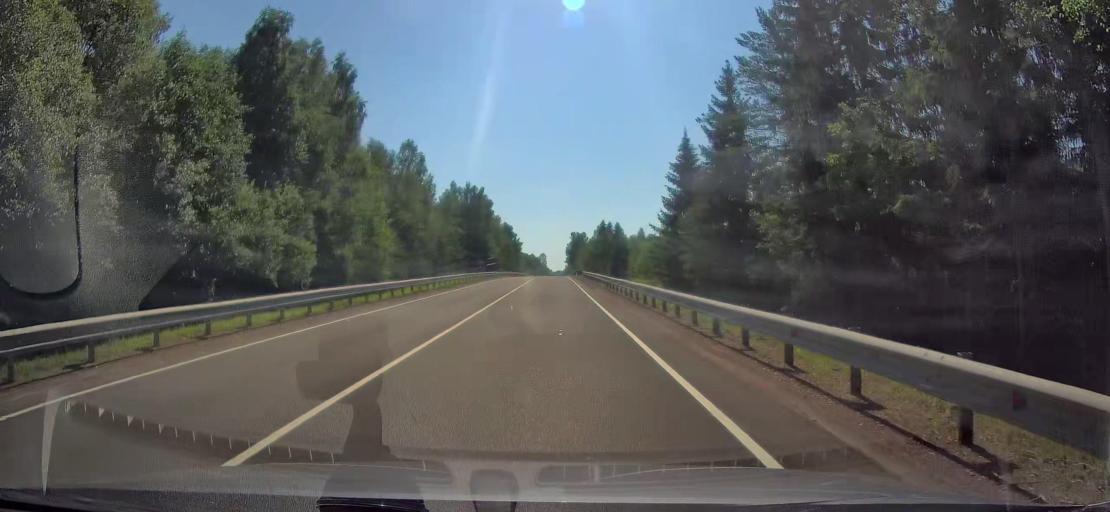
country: RU
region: Leningrad
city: Yefimovskiy
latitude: 59.4027
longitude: 34.7237
